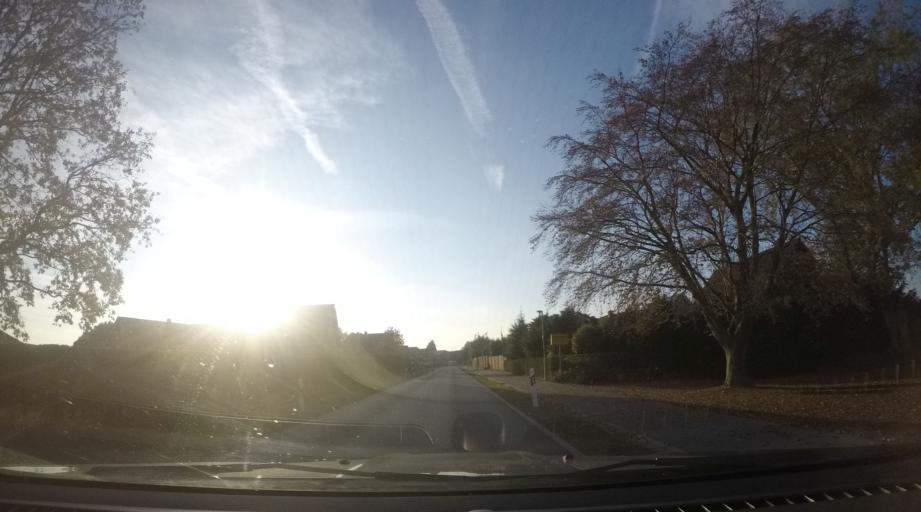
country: DE
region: North Rhine-Westphalia
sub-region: Regierungsbezirk Dusseldorf
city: Bocholt
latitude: 51.8160
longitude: 6.6350
